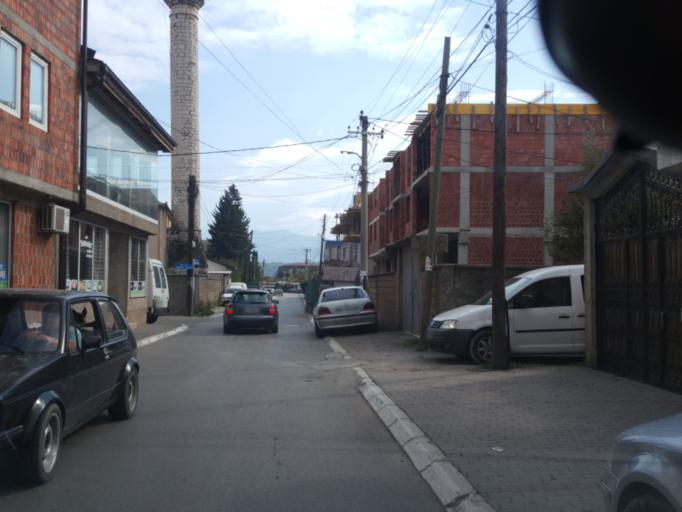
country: XK
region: Gjakova
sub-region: Komuna e Gjakoves
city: Gjakove
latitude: 42.3719
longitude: 20.4298
